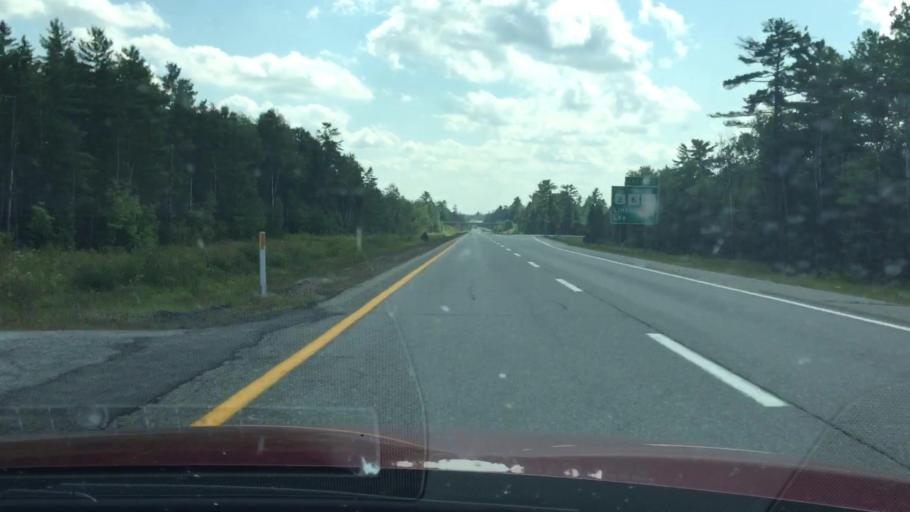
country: US
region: Maine
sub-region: Penobscot County
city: Lincoln
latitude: 45.3821
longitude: -68.6054
